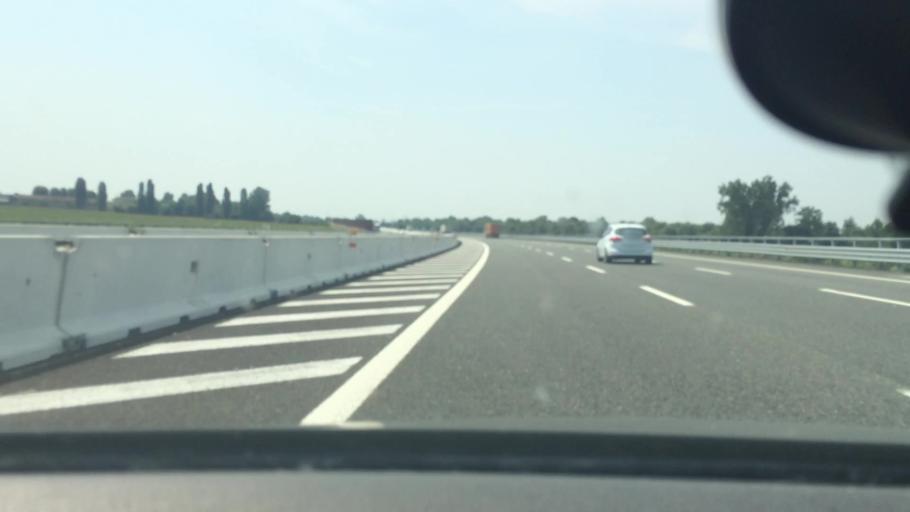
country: IT
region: Lombardy
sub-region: Provincia di Lodi
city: Cassino d'Alberi
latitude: 45.3876
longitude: 9.3757
